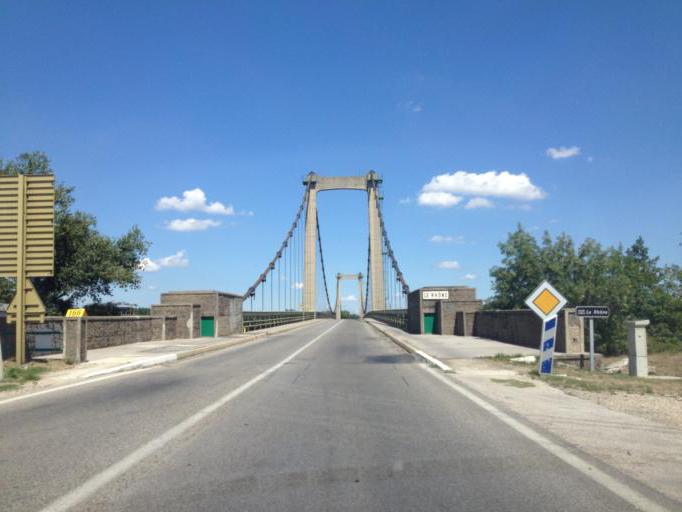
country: FR
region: Languedoc-Roussillon
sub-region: Departement du Gard
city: Montfaucon
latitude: 44.0698
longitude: 4.7677
